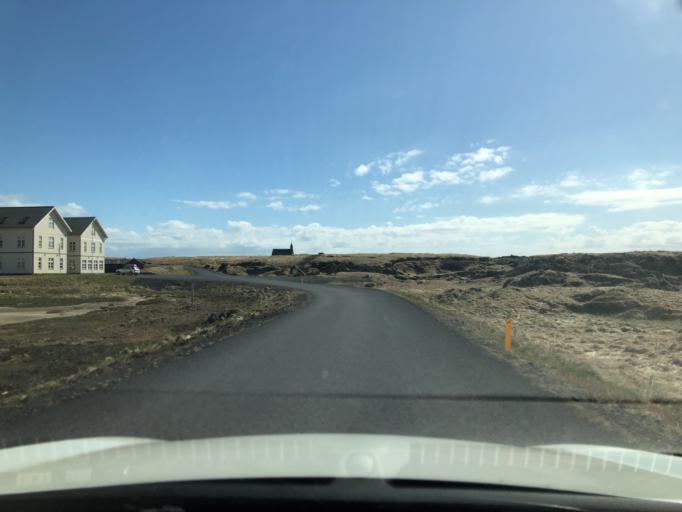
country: IS
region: West
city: Olafsvik
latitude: 64.8239
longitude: -23.3860
